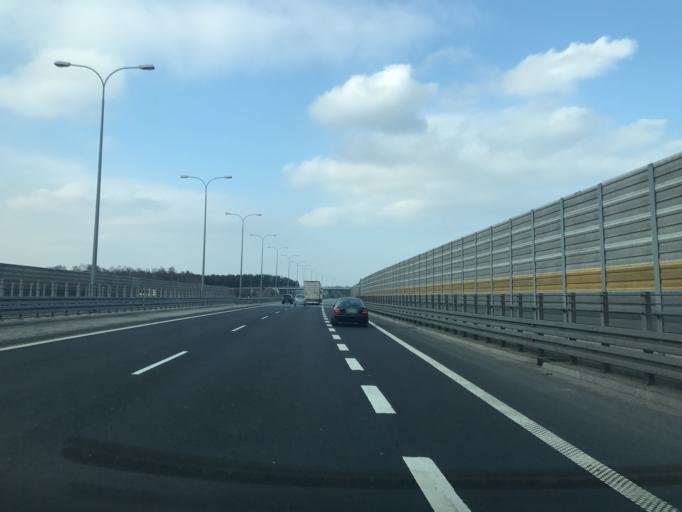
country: PL
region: Kujawsko-Pomorskie
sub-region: Powiat torunski
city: Lubicz Dolny
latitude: 53.0298
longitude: 18.7315
